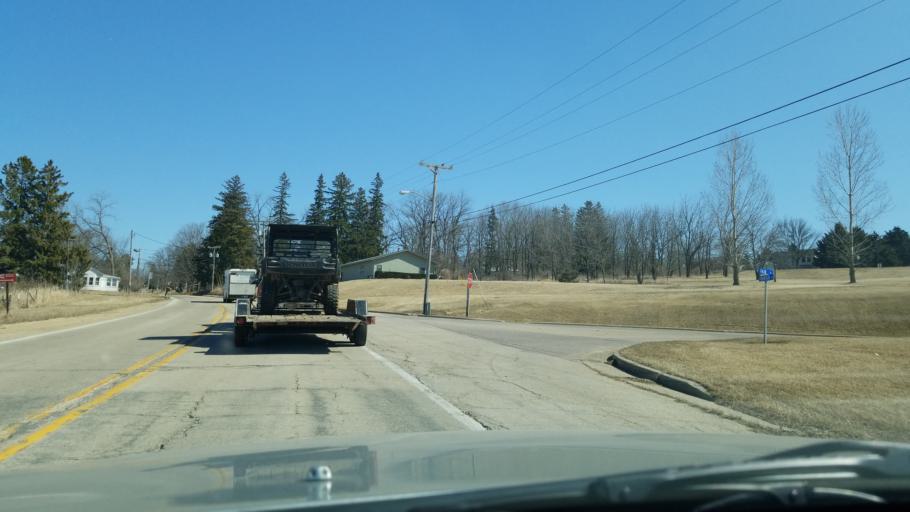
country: US
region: Wisconsin
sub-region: Iowa County
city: Mineral Point
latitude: 42.8605
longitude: -90.2000
